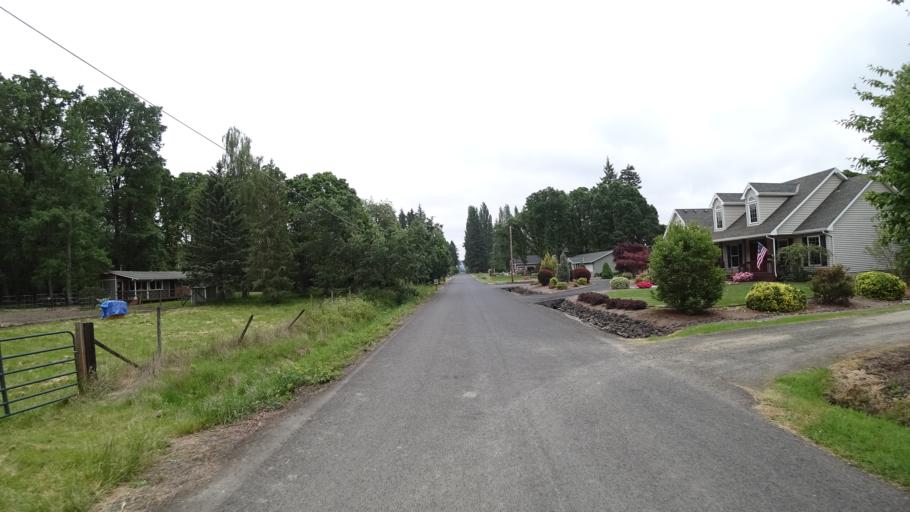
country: US
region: Oregon
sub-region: Washington County
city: Rockcreek
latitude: 45.5727
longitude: -122.8968
